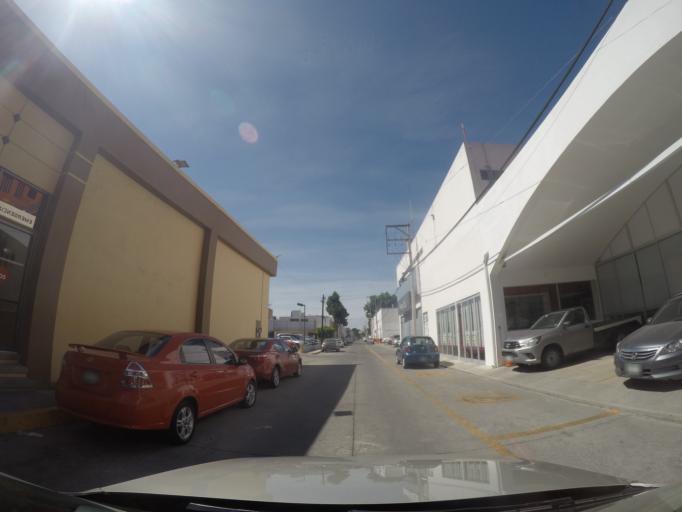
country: MX
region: San Luis Potosi
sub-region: San Luis Potosi
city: San Luis Potosi
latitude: 22.1492
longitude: -101.0080
